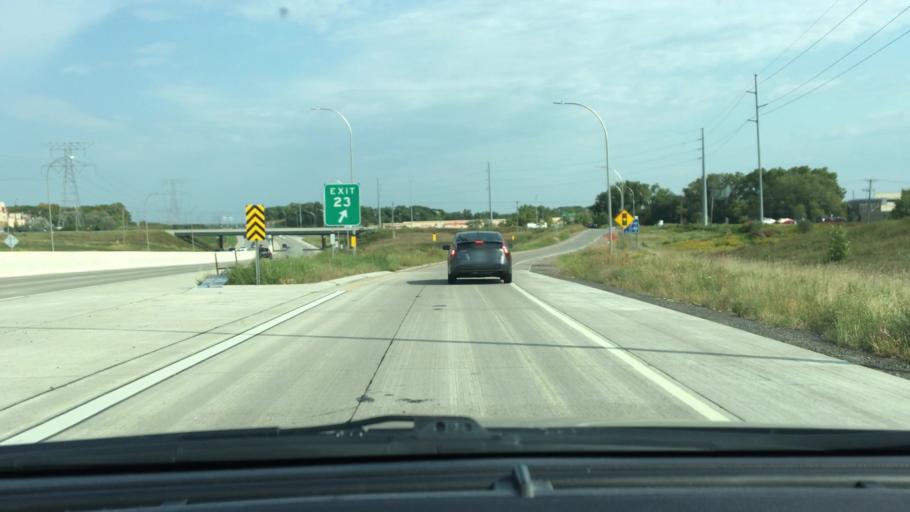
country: US
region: Minnesota
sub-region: Hennepin County
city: Plymouth
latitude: 45.0258
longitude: -93.4528
